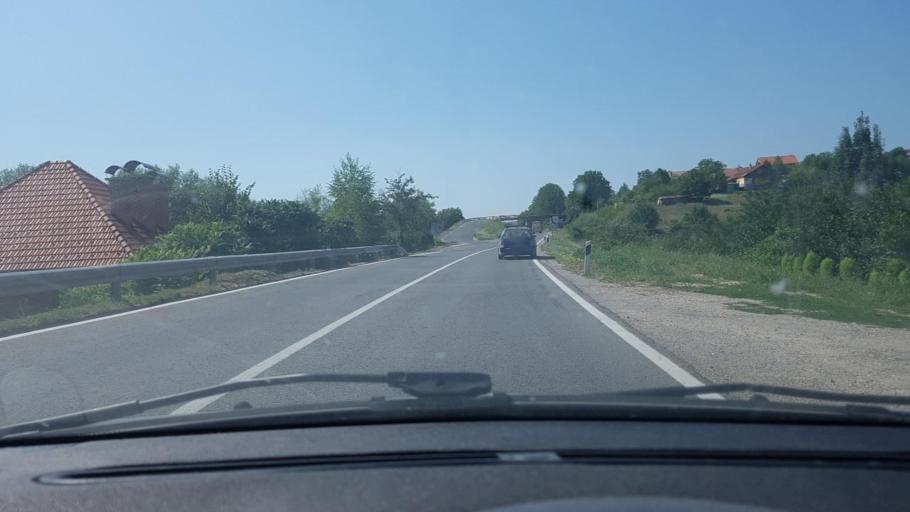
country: BA
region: Federation of Bosnia and Herzegovina
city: Bihac
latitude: 44.7986
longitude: 15.9136
